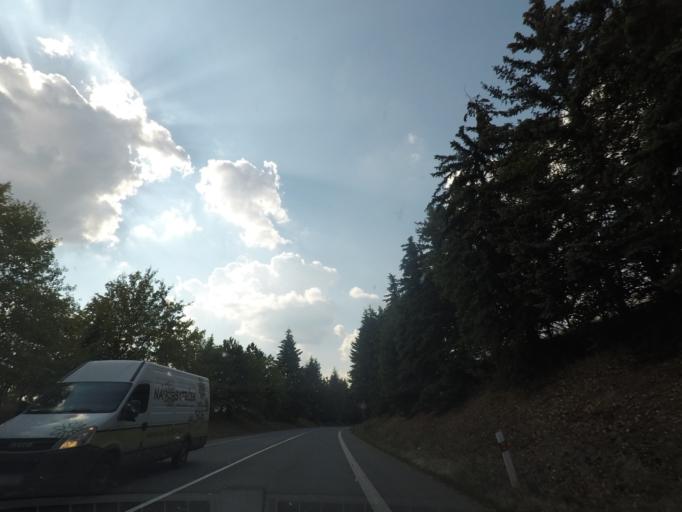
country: CZ
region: Kralovehradecky
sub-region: Okres Nachod
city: Jaromer
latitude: 50.4016
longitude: 15.8935
